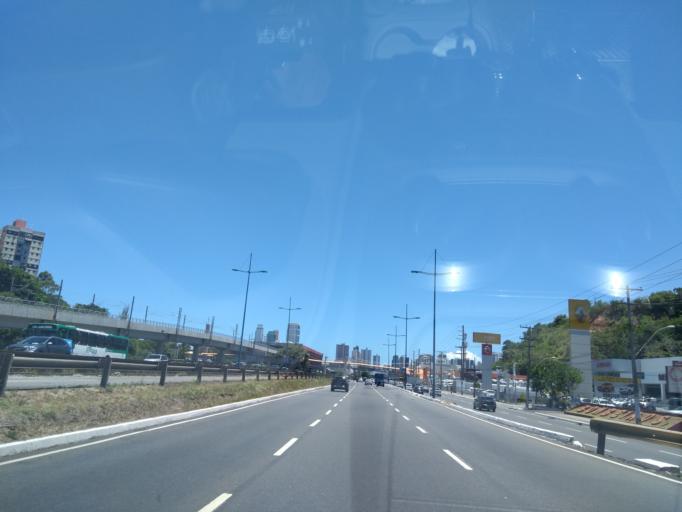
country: BR
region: Bahia
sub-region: Salvador
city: Salvador
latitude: -12.9774
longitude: -38.4748
